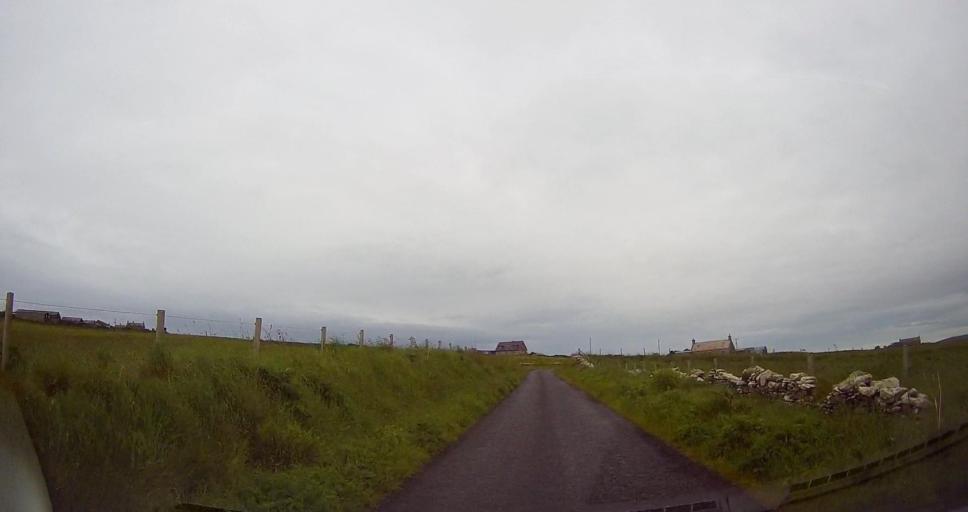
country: GB
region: Scotland
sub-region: Orkney Islands
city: Stromness
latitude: 59.1256
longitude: -3.2848
